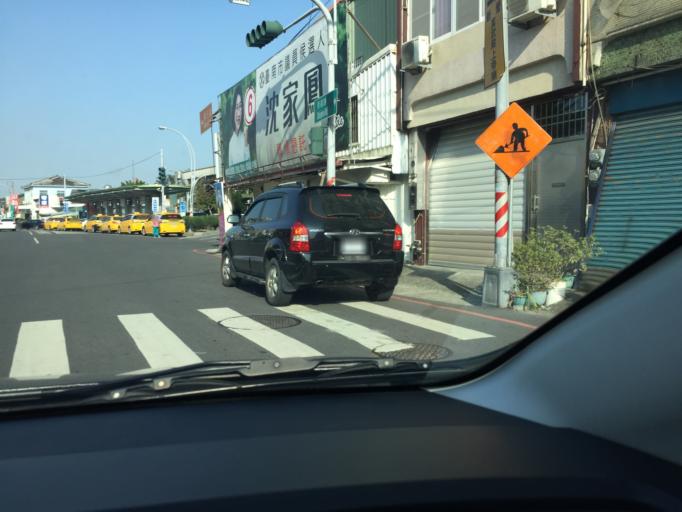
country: TW
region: Taiwan
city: Xinying
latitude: 23.3064
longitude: 120.3224
